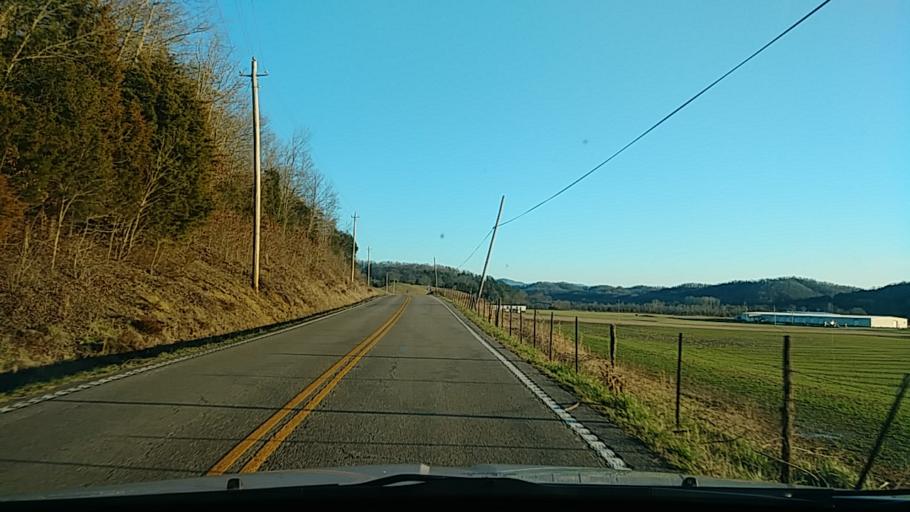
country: US
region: Tennessee
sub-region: Greene County
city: Mosheim
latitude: 36.1160
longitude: -83.0802
